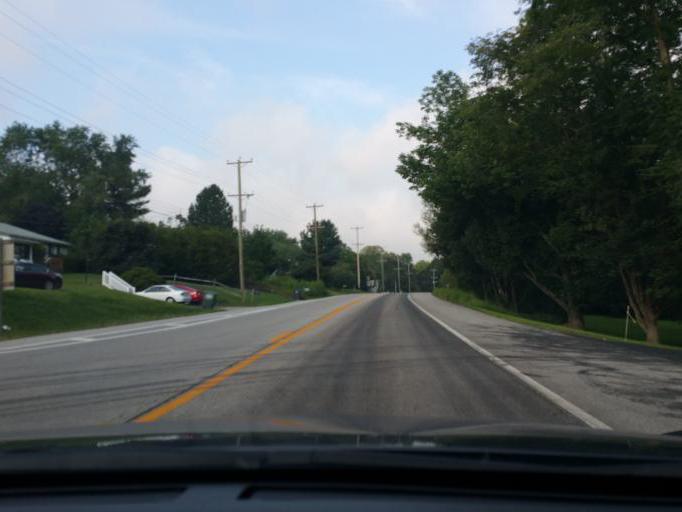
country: US
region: Maryland
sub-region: Cecil County
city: Rising Sun
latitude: 39.6946
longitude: -76.0951
